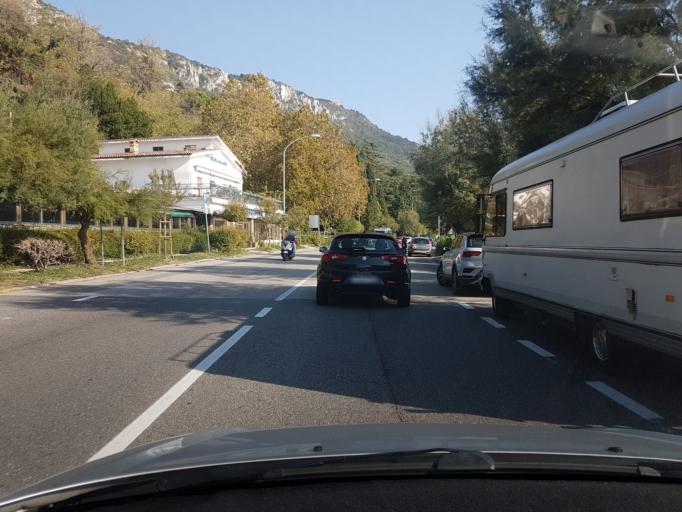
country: IT
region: Friuli Venezia Giulia
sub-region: Provincia di Trieste
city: Prosecco-Contovello
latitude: 45.6969
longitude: 13.7324
